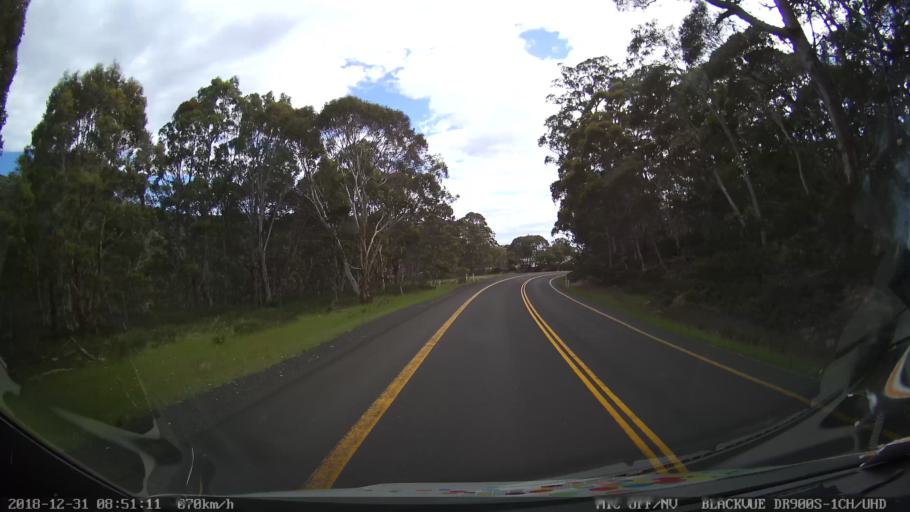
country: AU
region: New South Wales
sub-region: Snowy River
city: Jindabyne
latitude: -36.3479
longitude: 148.5243
